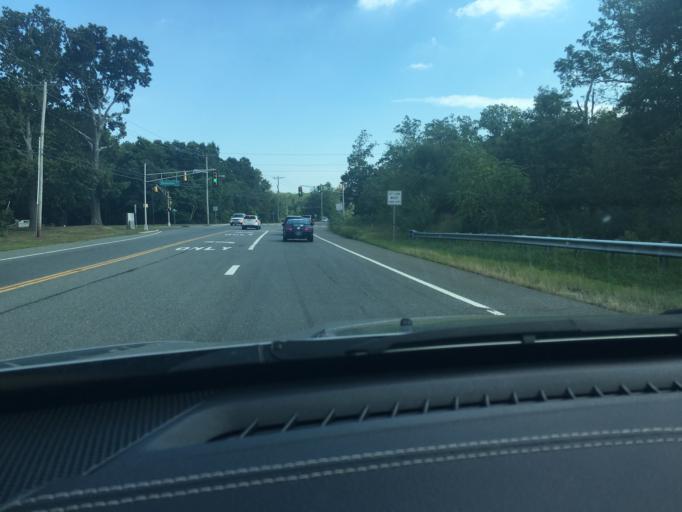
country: US
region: New Jersey
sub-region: Ocean County
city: Leisure Knoll
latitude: 40.0270
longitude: -74.2760
